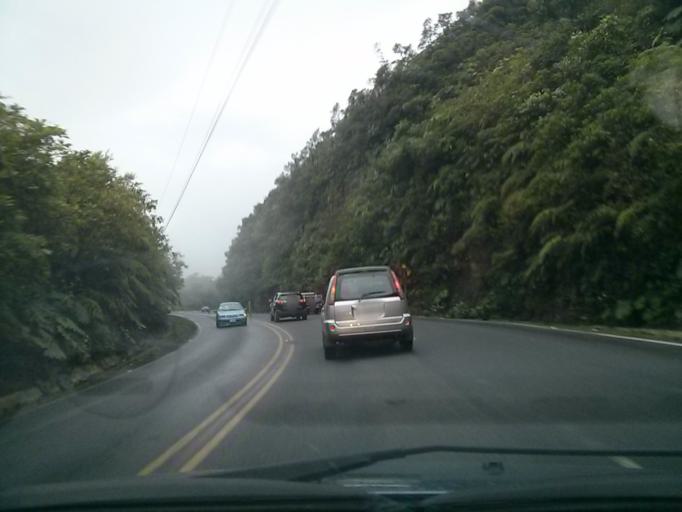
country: CR
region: Heredia
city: Angeles
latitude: 10.0544
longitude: -84.0054
